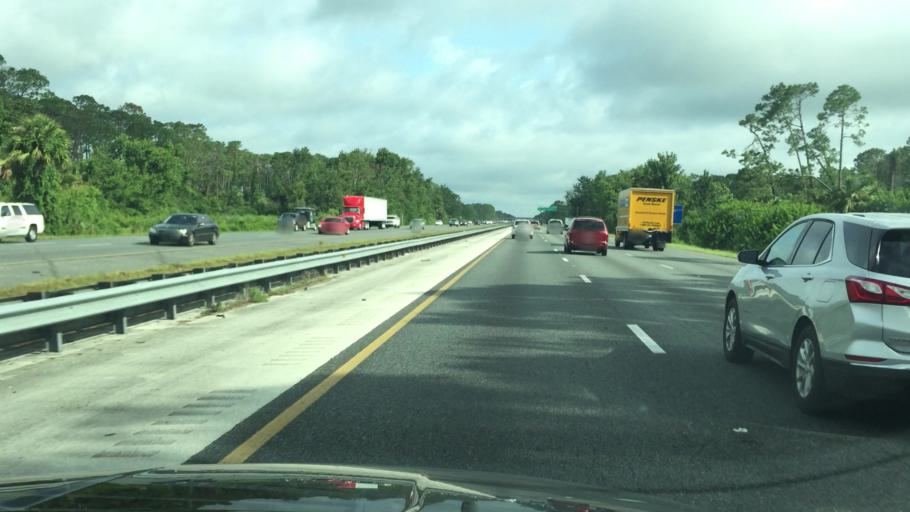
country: US
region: Florida
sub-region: Flagler County
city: Flagler Beach
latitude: 29.3922
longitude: -81.1501
